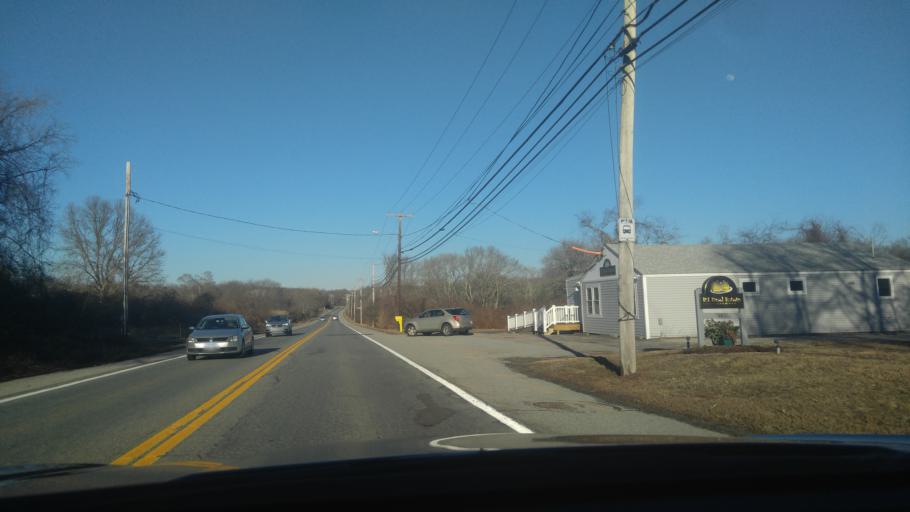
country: US
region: Rhode Island
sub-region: Washington County
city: Narragansett Pier
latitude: 41.4550
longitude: -71.4405
